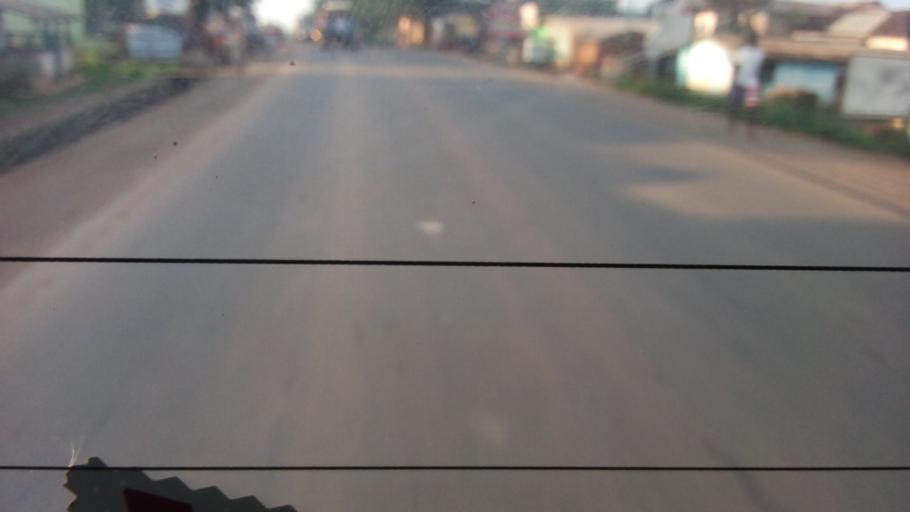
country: GH
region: Western
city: Tarkwa
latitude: 5.1545
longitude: -2.0760
